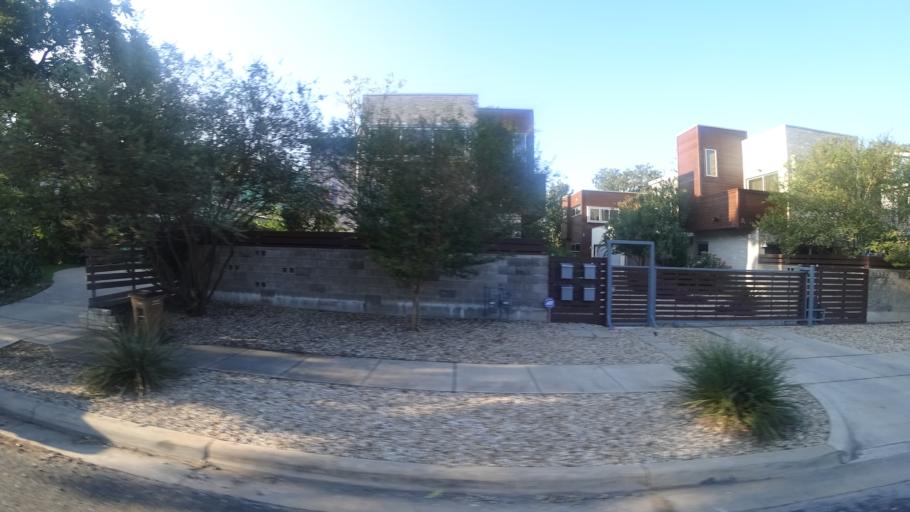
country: US
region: Texas
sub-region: Travis County
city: Austin
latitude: 30.2556
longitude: -97.7356
